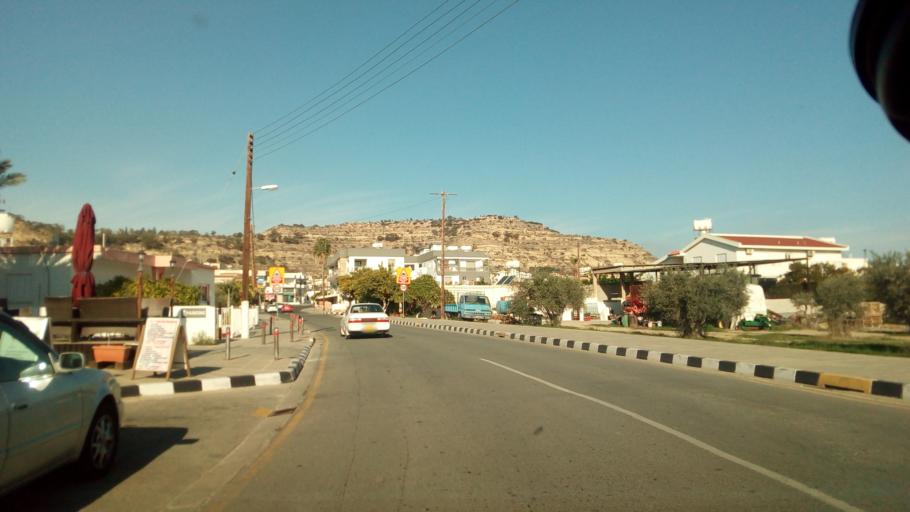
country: CY
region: Larnaka
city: Voroklini
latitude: 34.9831
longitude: 33.6558
